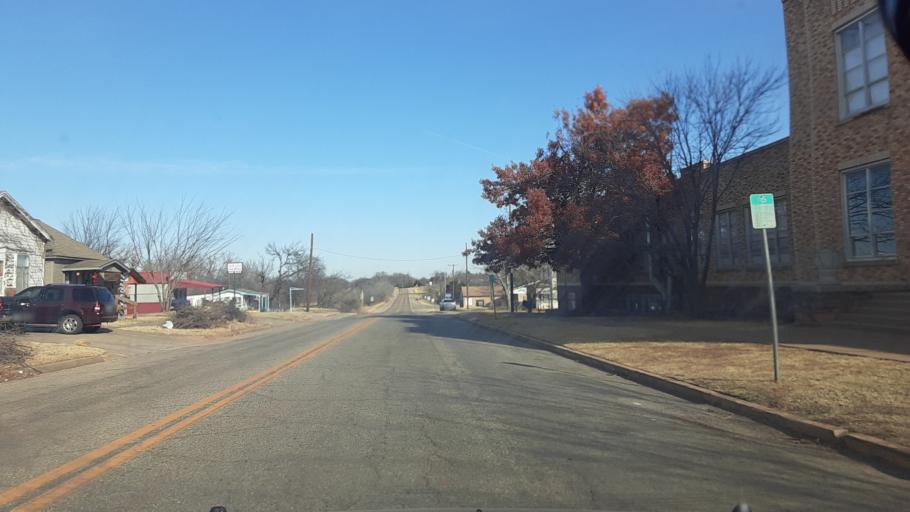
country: US
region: Oklahoma
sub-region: Logan County
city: Guthrie
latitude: 35.8868
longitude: -97.4240
